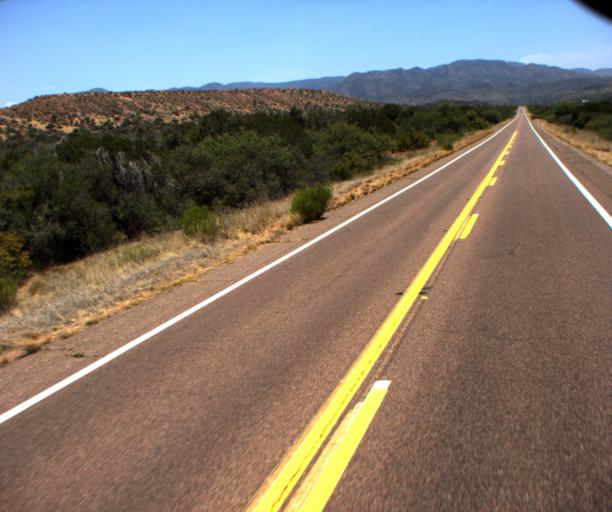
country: US
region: Arizona
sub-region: Gila County
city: Tonto Basin
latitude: 34.0245
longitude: -111.3425
